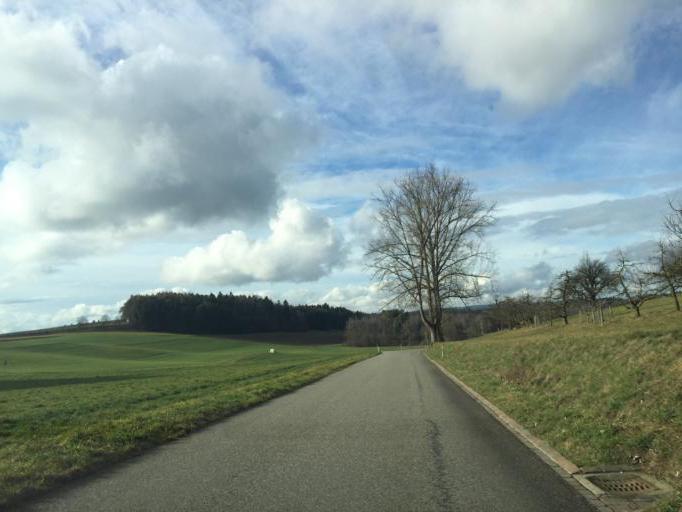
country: CH
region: Zurich
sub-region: Bezirk Andelfingen
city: Kleinandelfingen
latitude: 47.6183
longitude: 8.7221
